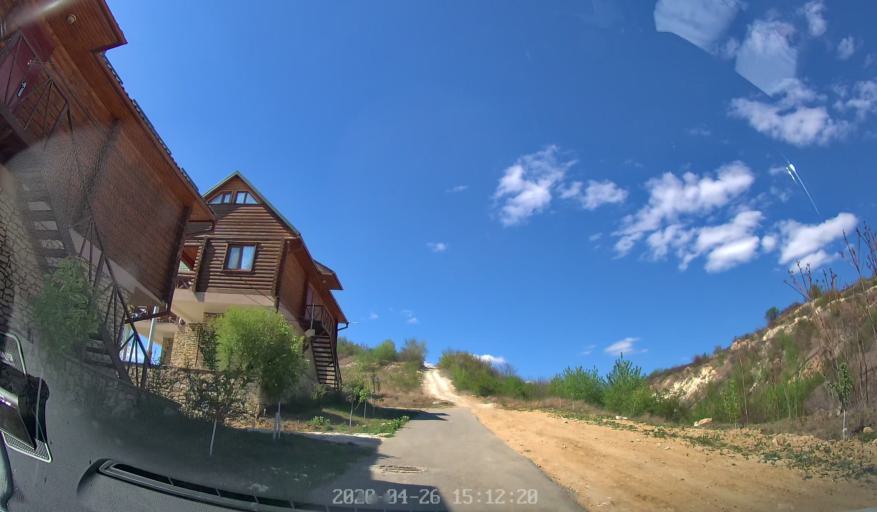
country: MD
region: Telenesti
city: Cocieri
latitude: 47.3634
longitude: 29.0987
